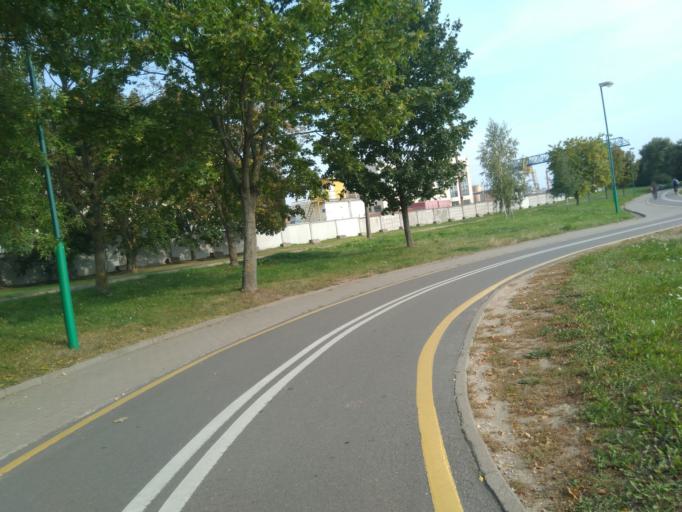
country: BY
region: Minsk
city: Minsk
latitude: 53.8823
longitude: 27.5746
